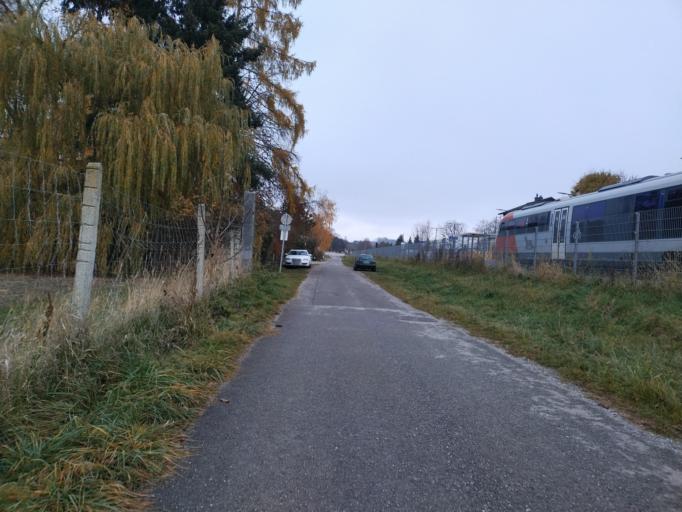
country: AT
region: Lower Austria
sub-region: Politischer Bezirk Neunkirchen
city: Pitten
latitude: 47.7165
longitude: 16.1789
